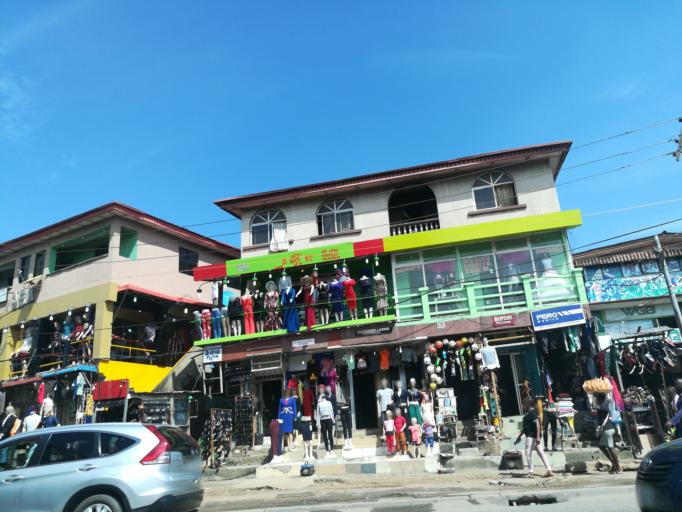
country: NG
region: Lagos
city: Ikeja
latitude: 6.5982
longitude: 3.3424
